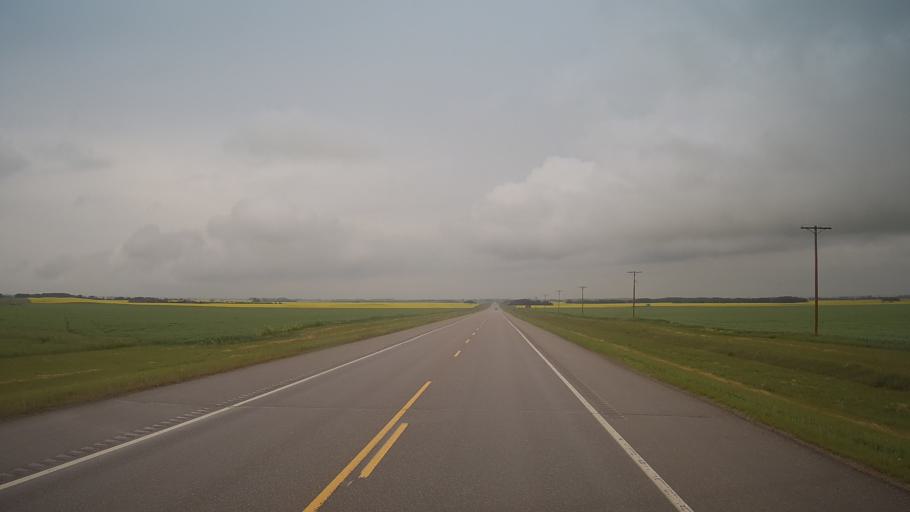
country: CA
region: Saskatchewan
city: Wilkie
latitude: 52.4201
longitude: -108.8942
